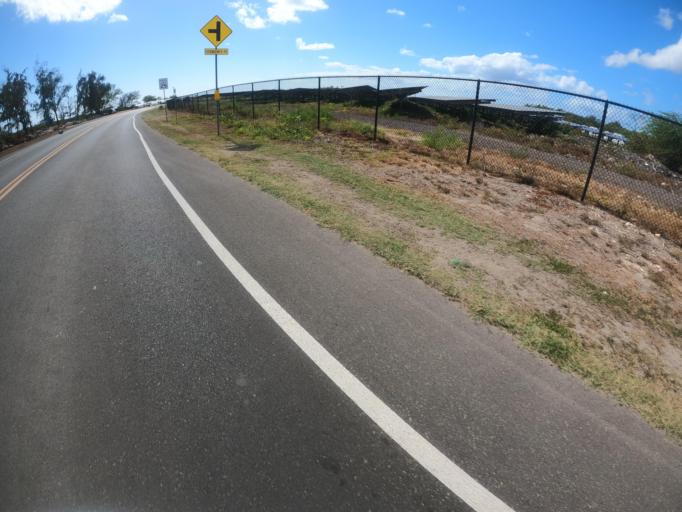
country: US
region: Hawaii
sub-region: Honolulu County
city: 'Ewa Villages
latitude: 21.3021
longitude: -158.0583
